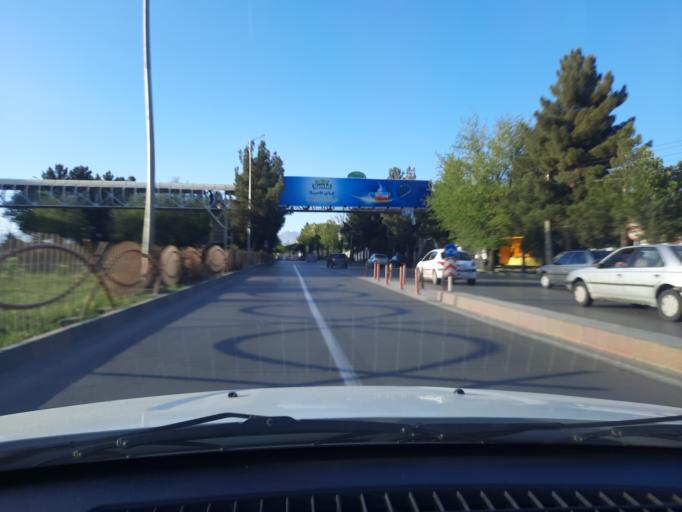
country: IR
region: Qazvin
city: Qazvin
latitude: 36.2774
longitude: 50.0242
